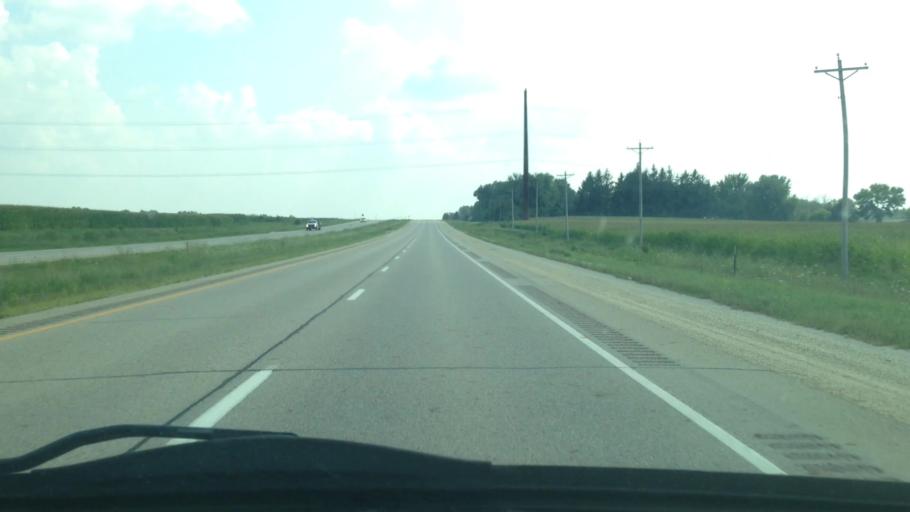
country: US
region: Iowa
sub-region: Bremer County
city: Denver
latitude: 42.5951
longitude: -92.3374
